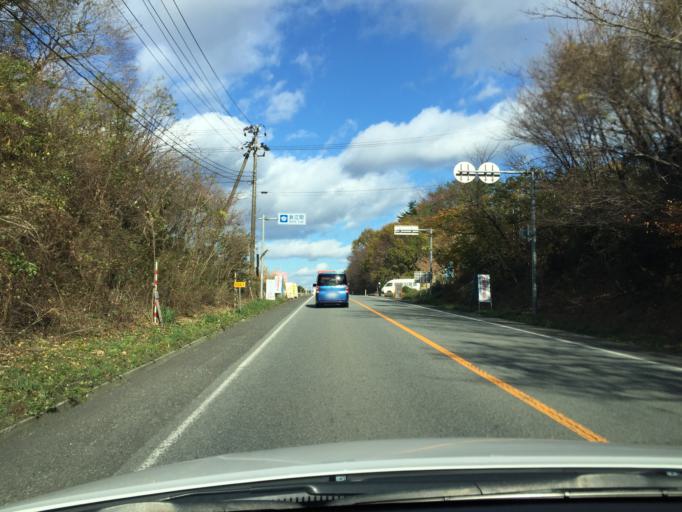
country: JP
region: Fukushima
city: Namie
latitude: 37.4756
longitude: 141.0077
